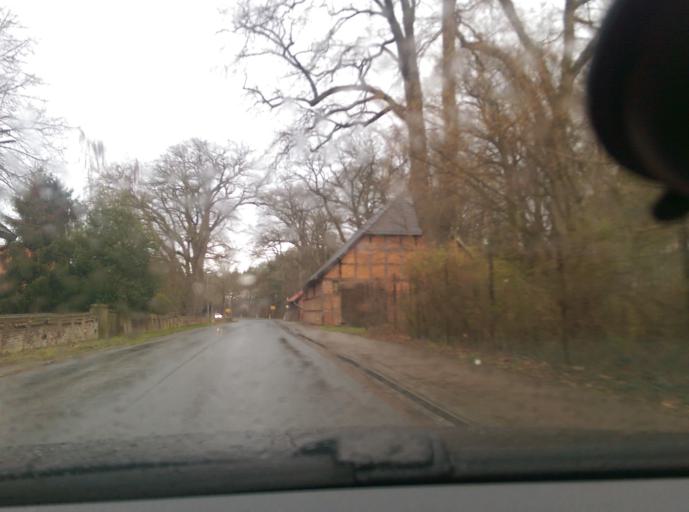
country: DE
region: Lower Saxony
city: Schwarmstedt
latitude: 52.6601
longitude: 9.6171
